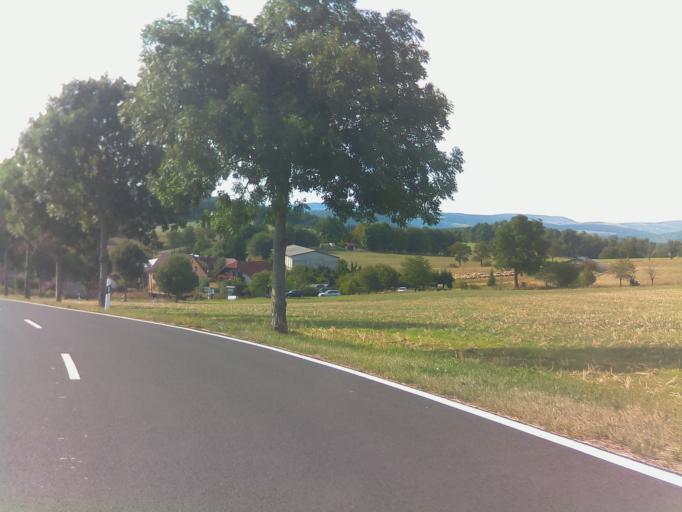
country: DE
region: Thuringia
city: Stepfershausen
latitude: 50.5795
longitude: 10.2669
